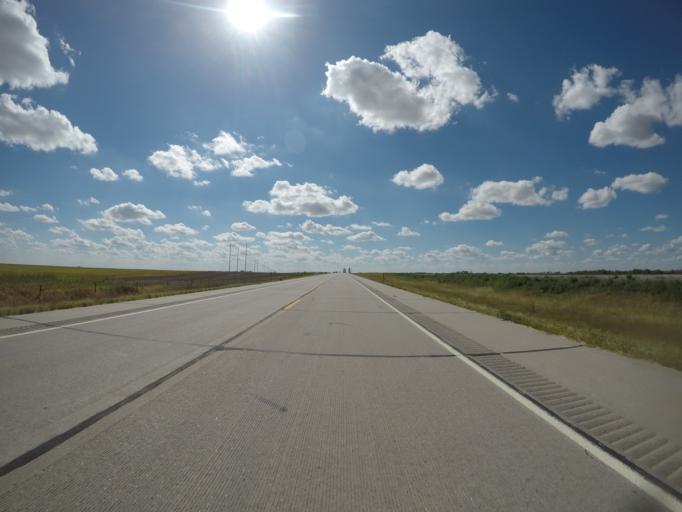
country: US
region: Colorado
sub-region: Phillips County
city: Holyoke
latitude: 40.6077
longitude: -102.4430
